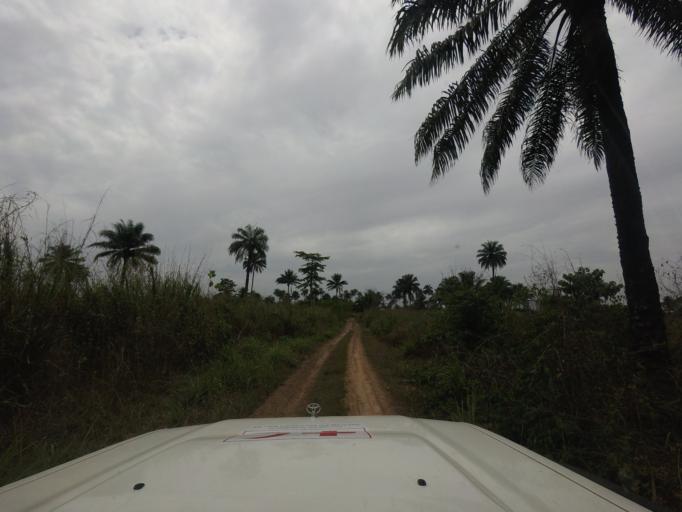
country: GN
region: Nzerekore
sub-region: Prefecture de Guekedou
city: Gueckedou
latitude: 8.4267
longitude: -10.2474
